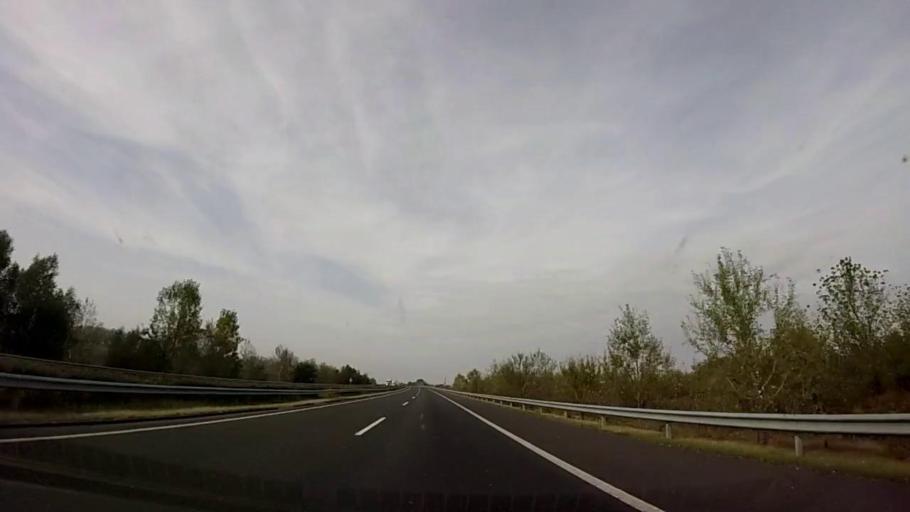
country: HU
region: Somogy
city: Balatonfenyves
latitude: 46.7032
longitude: 17.4919
